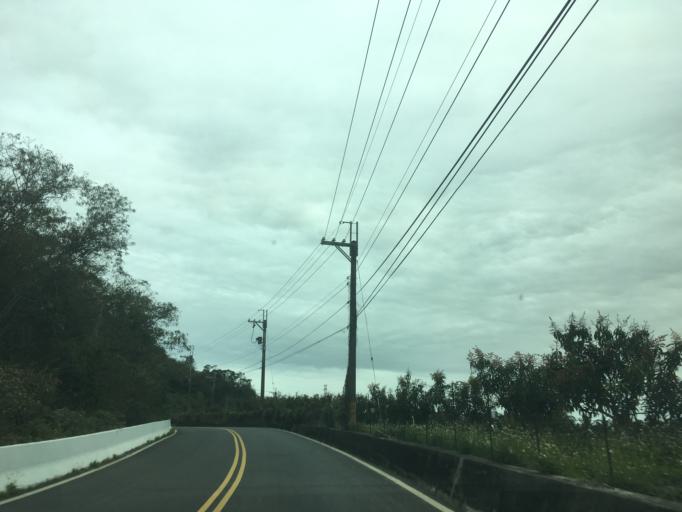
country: TW
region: Taiwan
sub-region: Taitung
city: Taitung
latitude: 22.8151
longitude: 121.1383
